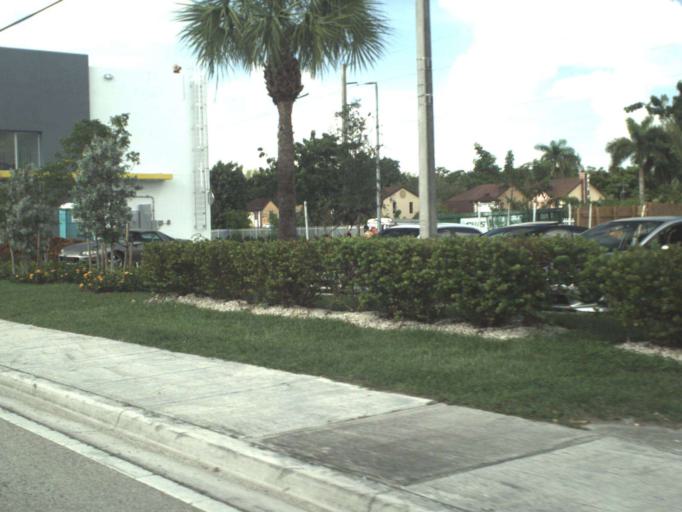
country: US
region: Florida
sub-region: Miami-Dade County
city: Ojus
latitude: 25.9410
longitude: -80.1491
